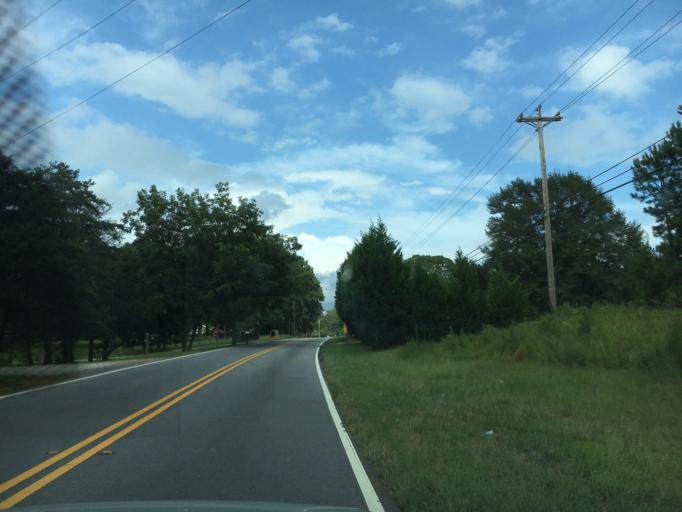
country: US
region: Georgia
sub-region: Rockdale County
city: Lakeview Estates
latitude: 33.7577
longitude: -84.0145
